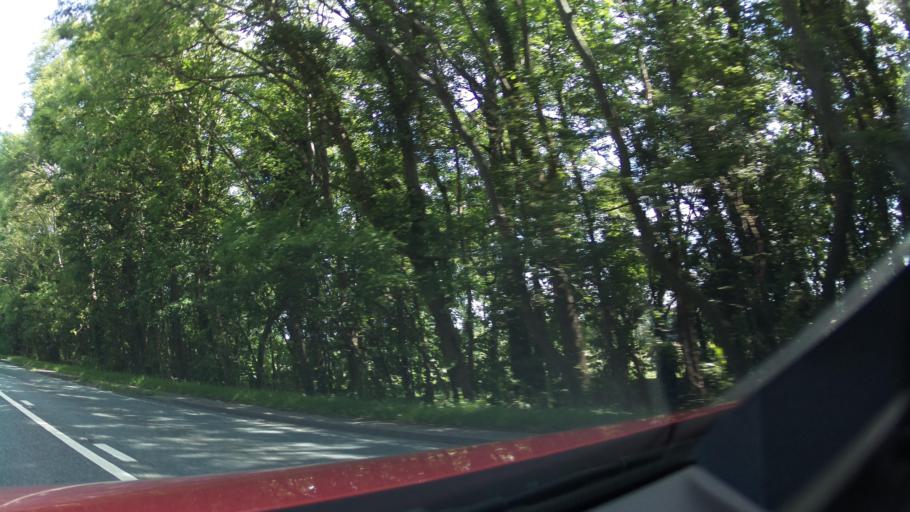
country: GB
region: England
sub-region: Lincolnshire
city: Burton
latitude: 53.2647
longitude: -0.5391
